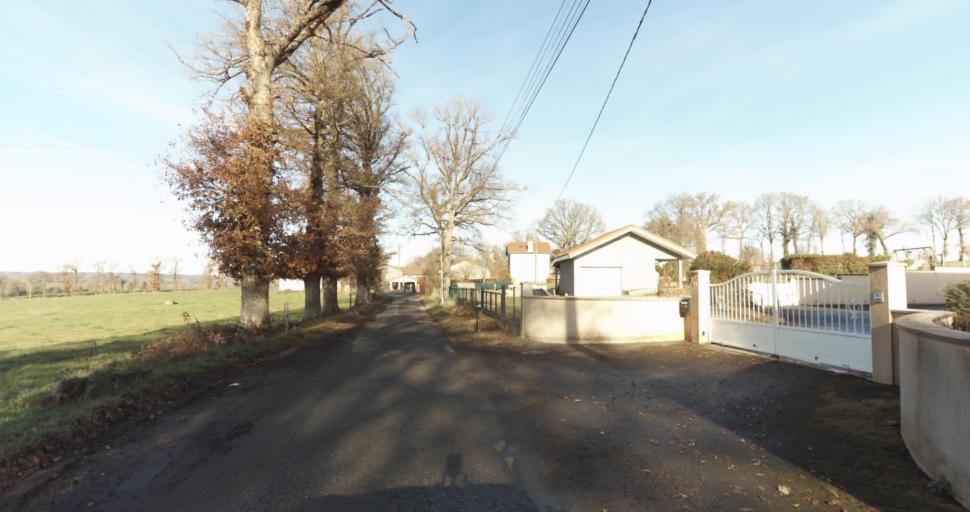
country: FR
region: Limousin
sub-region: Departement de la Haute-Vienne
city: Aixe-sur-Vienne
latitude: 45.7844
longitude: 1.1161
